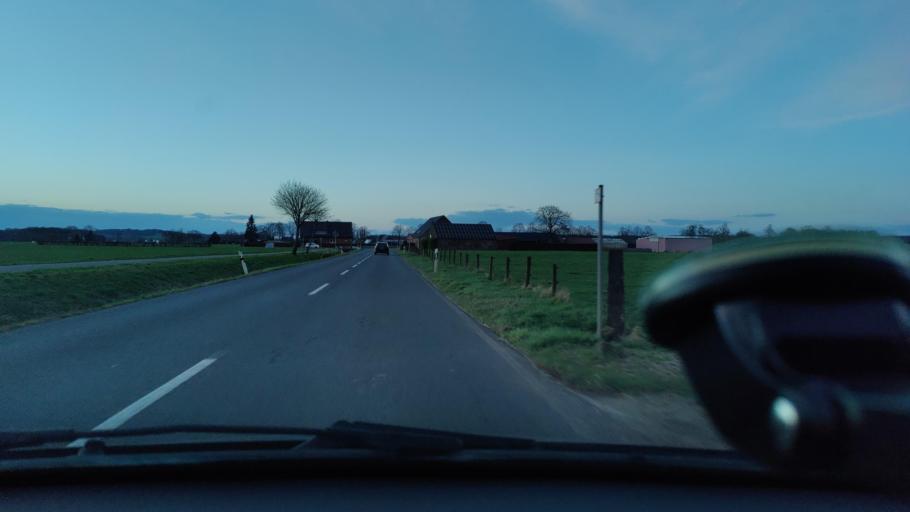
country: DE
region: North Rhine-Westphalia
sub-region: Regierungsbezirk Dusseldorf
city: Xanten
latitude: 51.6051
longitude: 6.4534
